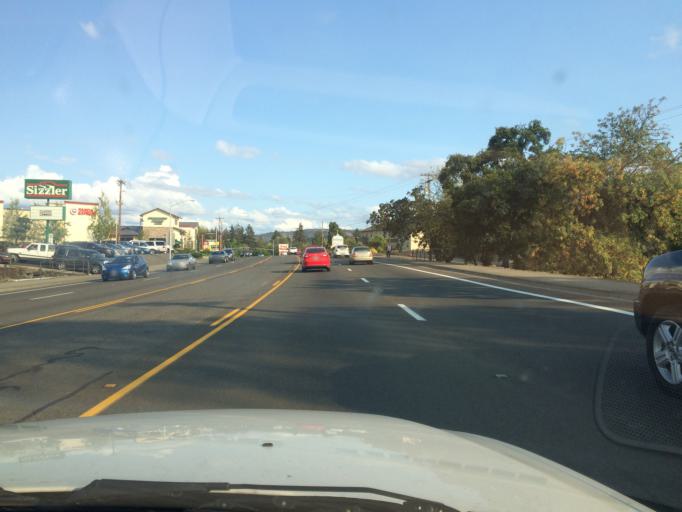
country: US
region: Oregon
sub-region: Douglas County
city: Roseburg
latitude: 43.2311
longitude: -123.3724
